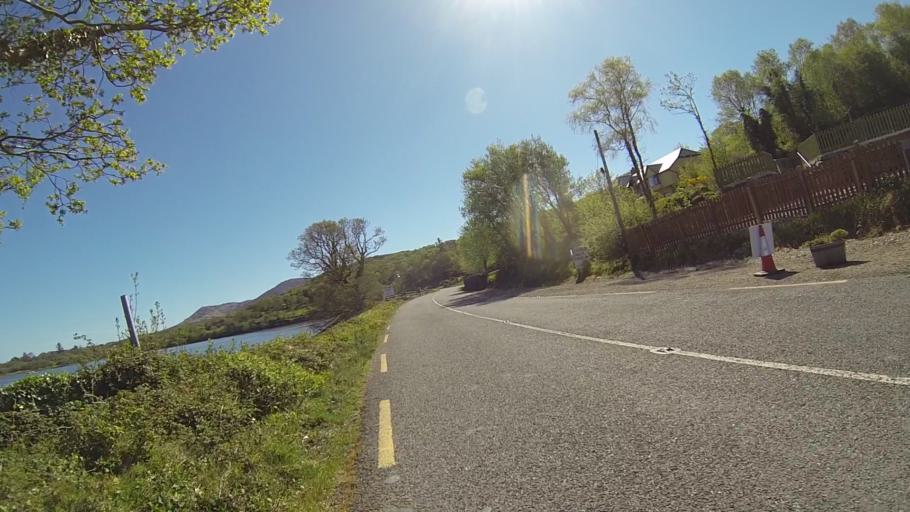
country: IE
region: Munster
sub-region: Ciarrai
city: Kenmare
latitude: 51.8448
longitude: -9.6505
